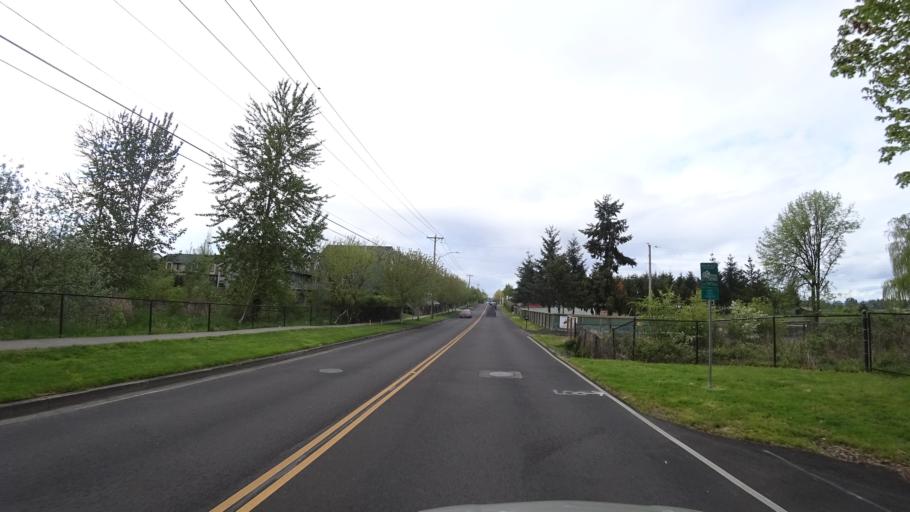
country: US
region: Oregon
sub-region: Washington County
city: Hillsboro
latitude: 45.5464
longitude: -122.9664
